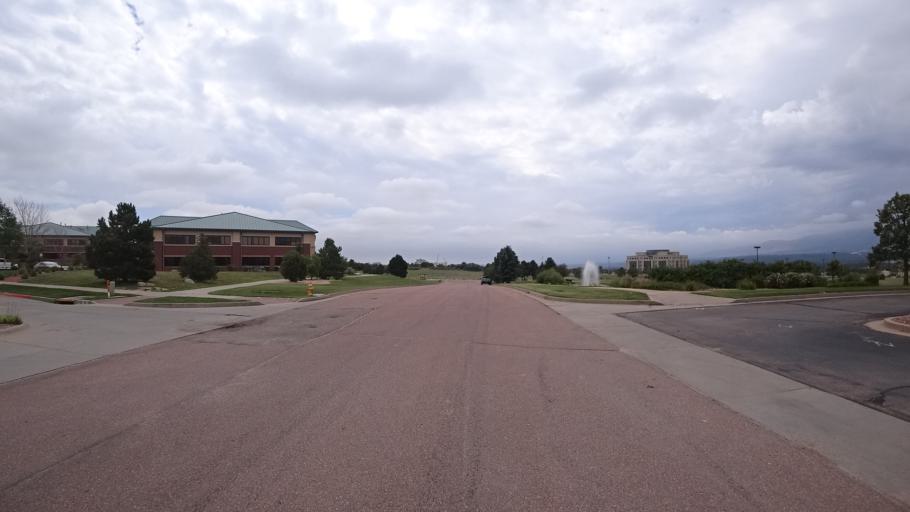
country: US
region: Colorado
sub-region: El Paso County
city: Gleneagle
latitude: 39.0114
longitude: -104.8164
